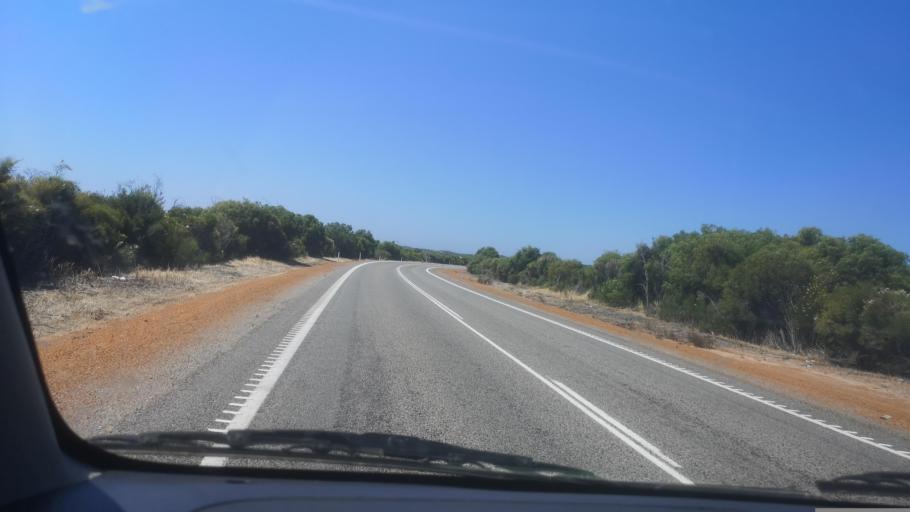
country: AU
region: Western Australia
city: Port Denison
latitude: -29.4926
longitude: 115.0032
